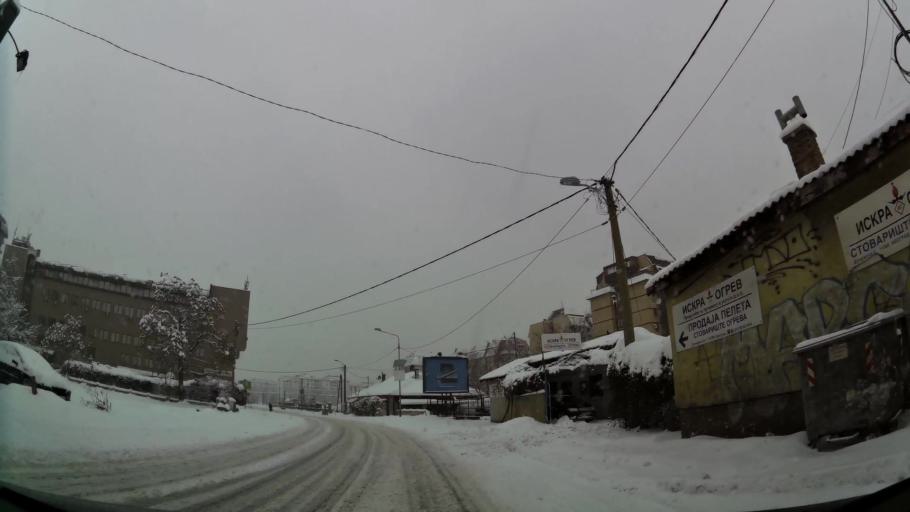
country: RS
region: Central Serbia
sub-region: Belgrade
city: Stari Grad
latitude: 44.8277
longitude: 20.4633
